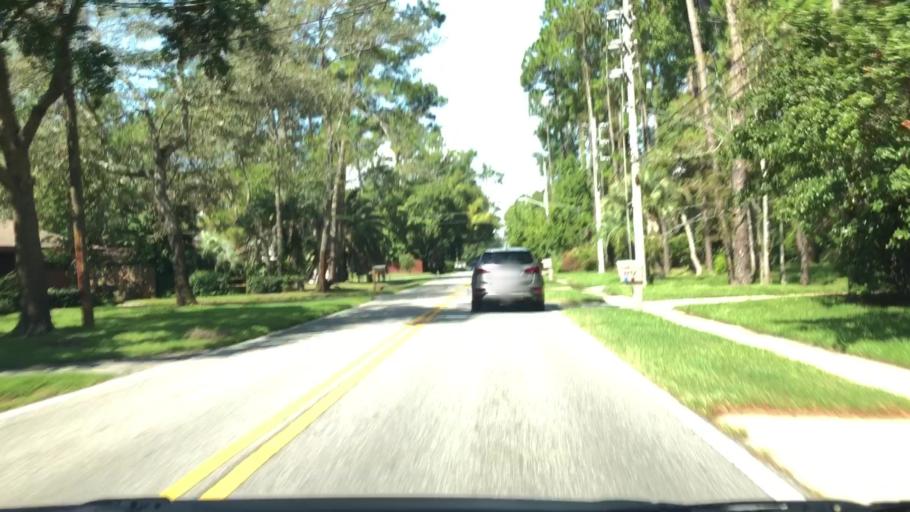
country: US
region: Florida
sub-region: Saint Johns County
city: Fruit Cove
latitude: 30.1849
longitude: -81.6214
